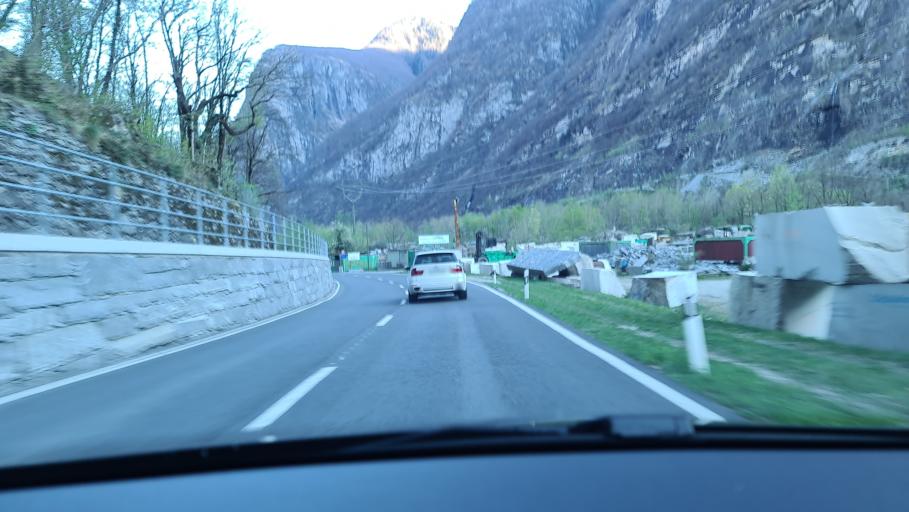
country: CH
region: Ticino
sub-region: Vallemaggia District
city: Cevio
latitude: 46.3033
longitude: 8.6184
